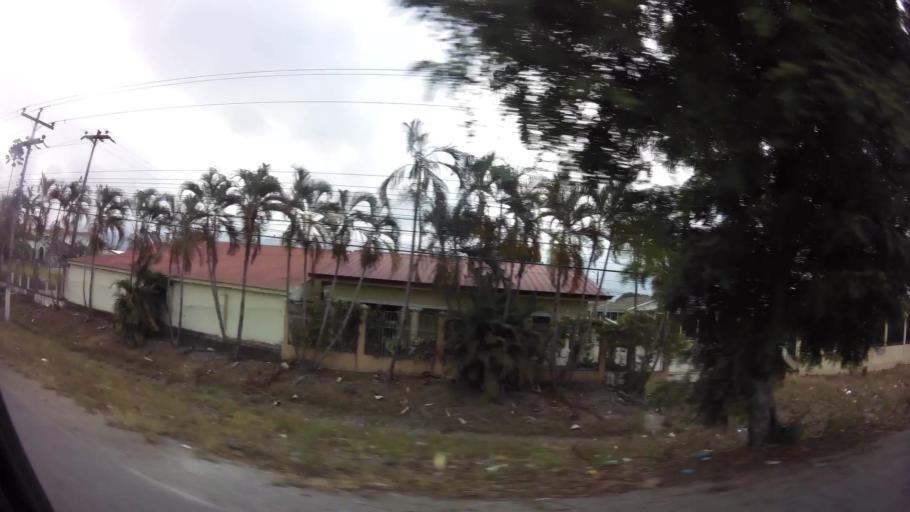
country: HN
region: Yoro
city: El Progreso
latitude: 15.4357
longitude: -87.7942
